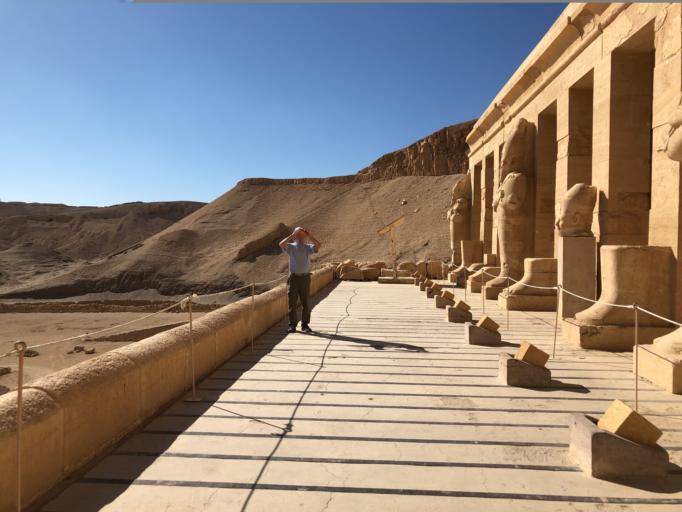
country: EG
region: Luxor
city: Luxor
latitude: 25.7382
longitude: 32.6067
